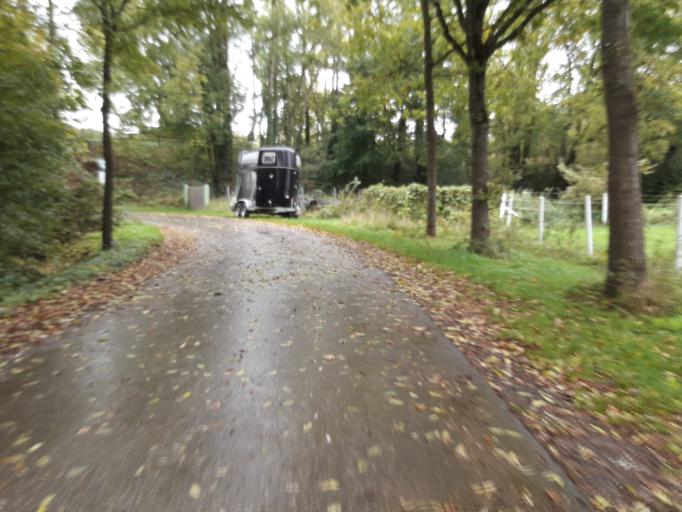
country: DE
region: North Rhine-Westphalia
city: Bad Lippspringe
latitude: 51.7688
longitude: 8.7879
